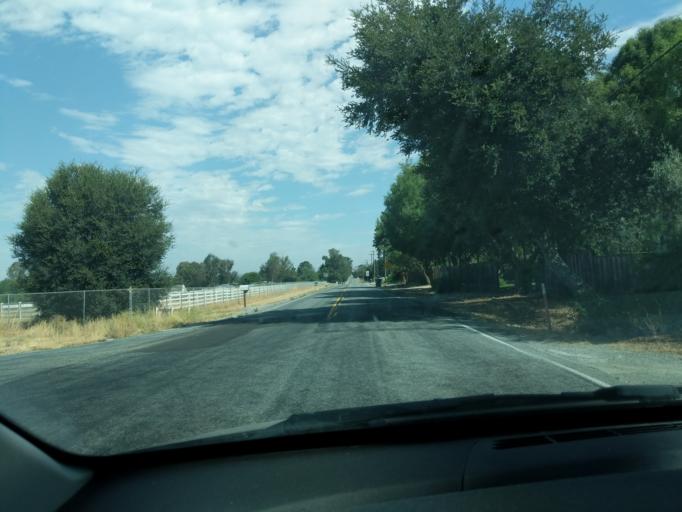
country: US
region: California
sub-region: Santa Clara County
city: Gilroy
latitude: 37.0633
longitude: -121.5538
